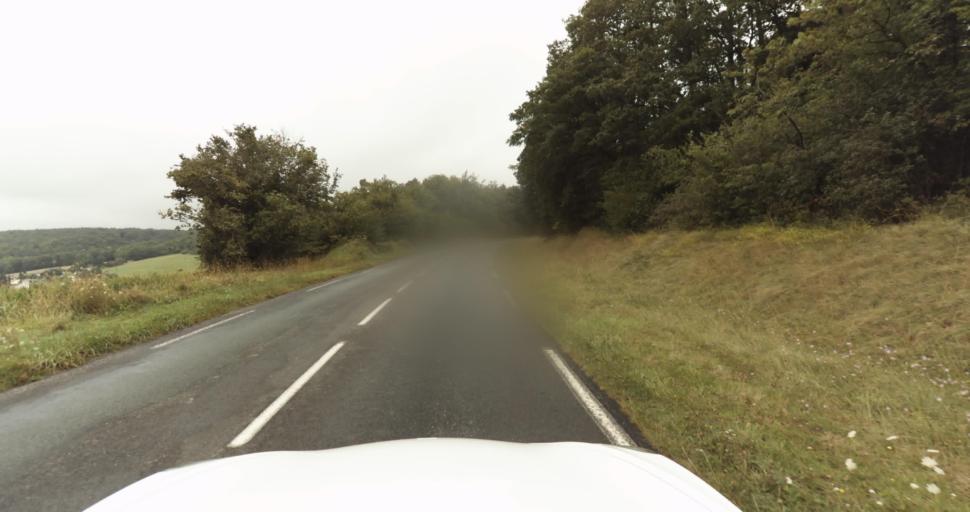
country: FR
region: Haute-Normandie
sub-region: Departement de l'Eure
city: Normanville
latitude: 49.0768
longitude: 1.1708
